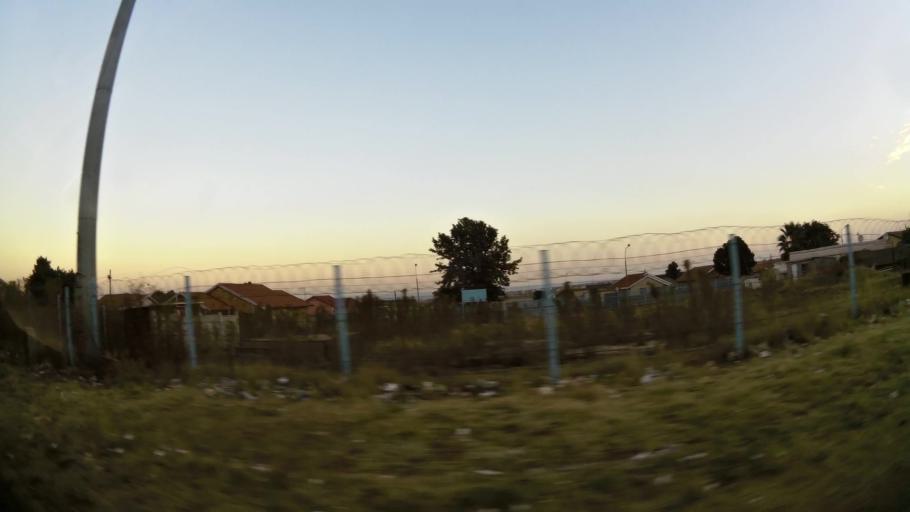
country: ZA
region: Gauteng
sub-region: West Rand District Municipality
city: Randfontein
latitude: -26.2102
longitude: 27.7169
